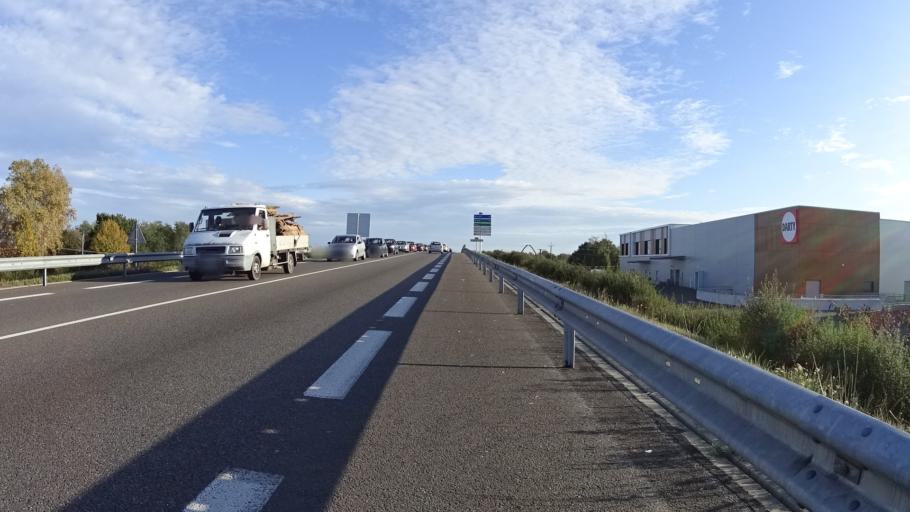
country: FR
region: Aquitaine
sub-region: Departement des Landes
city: Saint-Paul-les-Dax
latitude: 43.7288
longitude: -1.0373
